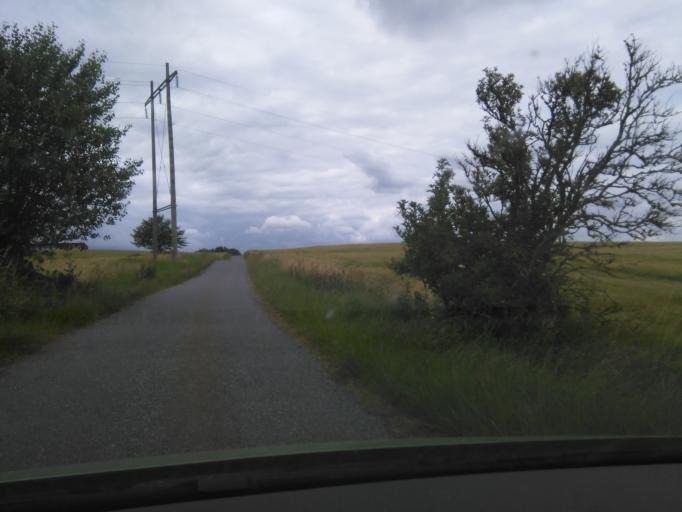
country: DK
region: Central Jutland
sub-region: Odder Kommune
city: Odder
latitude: 56.0074
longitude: 10.1435
